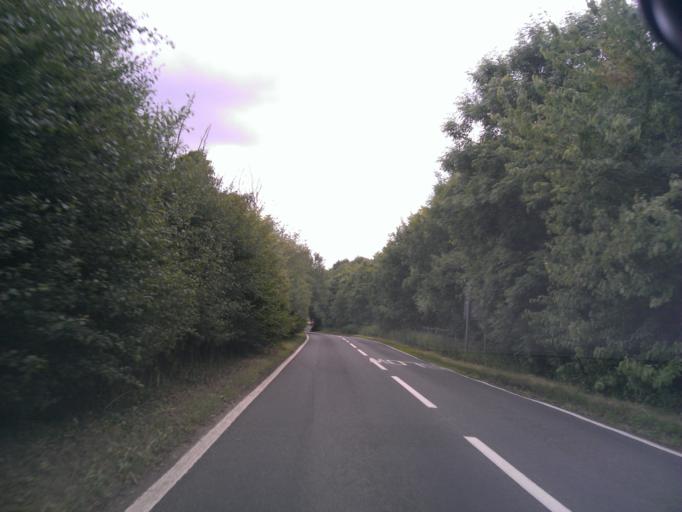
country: GB
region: England
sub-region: Essex
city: Witham
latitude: 51.8407
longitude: 0.6446
